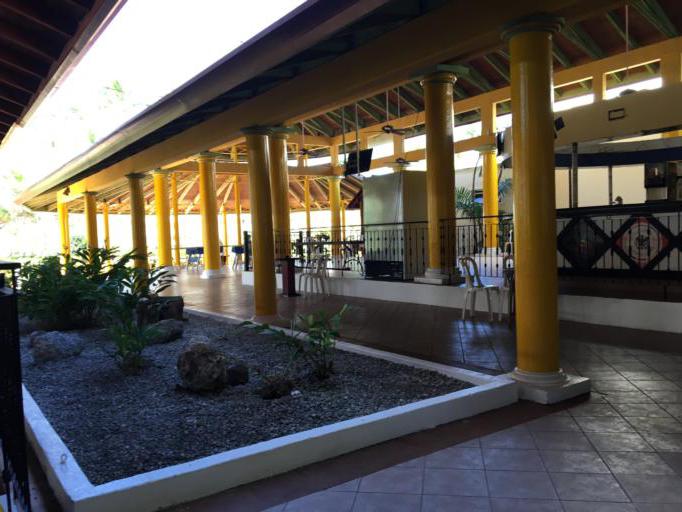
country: DO
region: San Juan
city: Punta Cana
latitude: 18.7083
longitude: -68.4430
